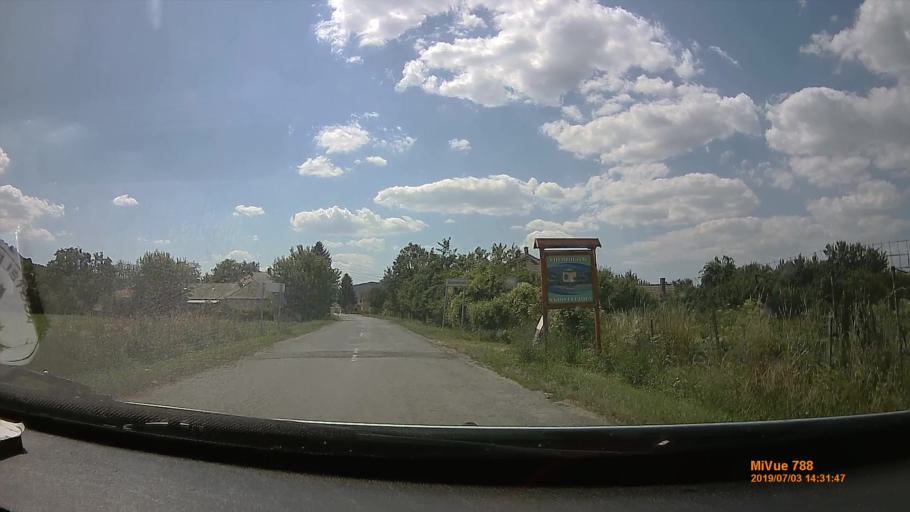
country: HU
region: Borsod-Abauj-Zemplen
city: Putnok
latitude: 48.2723
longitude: 20.4669
